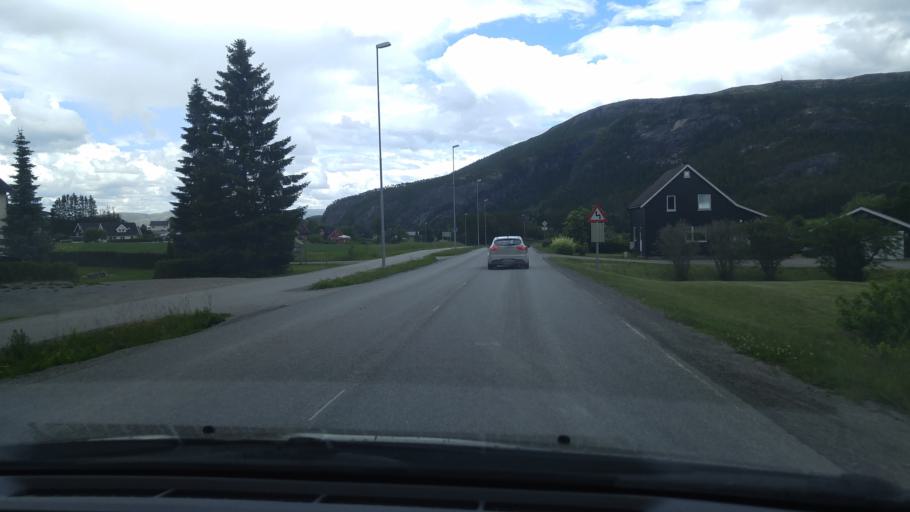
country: NO
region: Nord-Trondelag
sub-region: Namsos
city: Namsos
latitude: 64.4395
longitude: 11.5136
